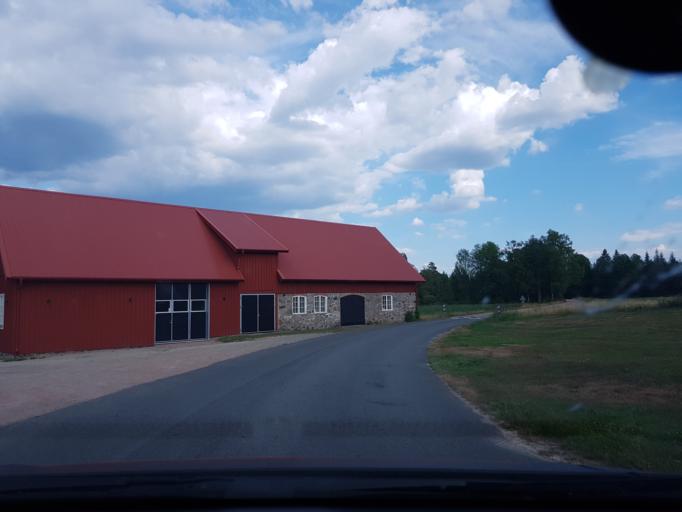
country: SE
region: Joenkoeping
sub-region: Gislaveds Kommun
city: Reftele
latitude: 57.2125
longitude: 13.5800
